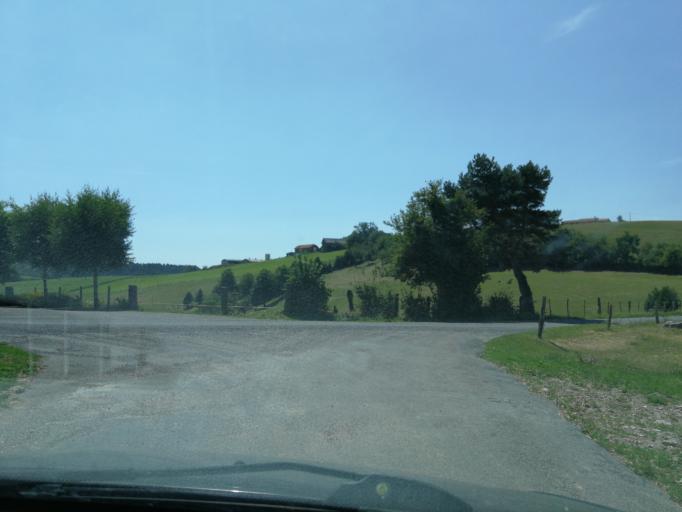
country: FR
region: Midi-Pyrenees
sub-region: Departement de l'Aveyron
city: Livinhac-le-Haut
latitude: 44.6696
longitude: 2.3247
